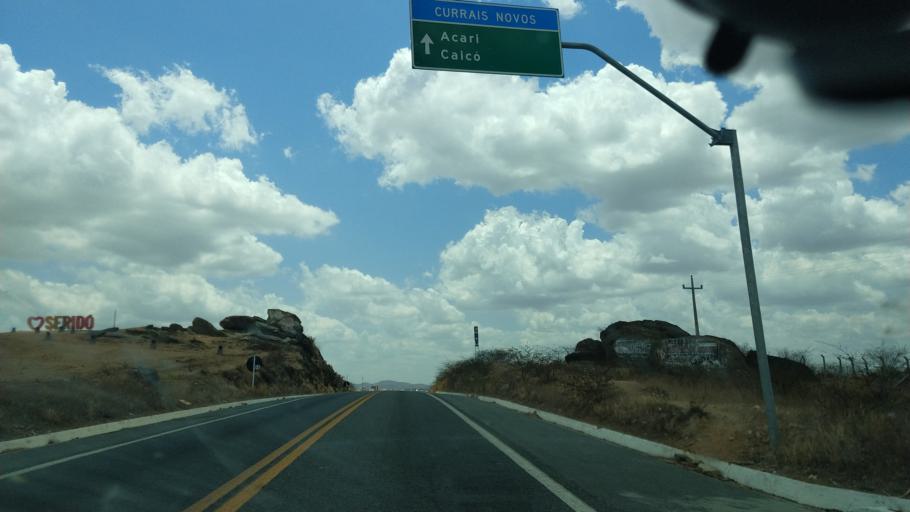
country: BR
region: Rio Grande do Norte
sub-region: Currais Novos
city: Currais Novos
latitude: -6.2575
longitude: -36.4968
